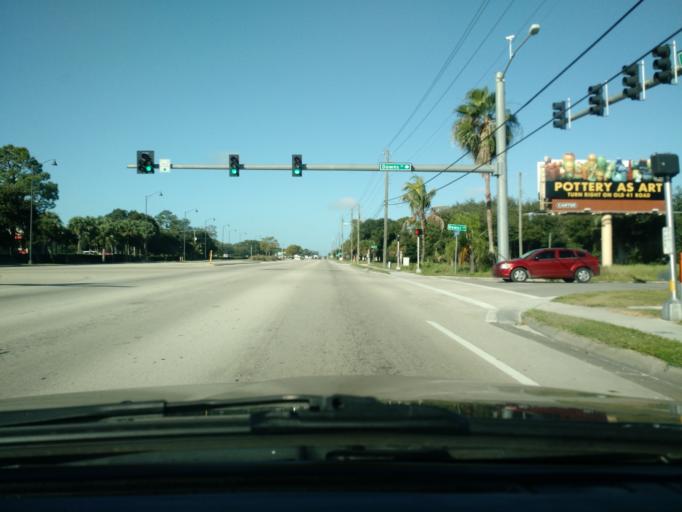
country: US
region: Florida
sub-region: Lee County
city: Bonita Springs
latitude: 26.3314
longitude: -81.7566
